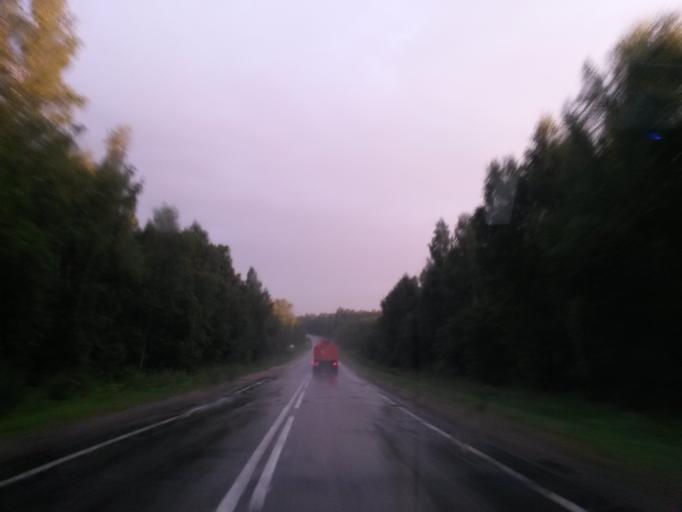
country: RU
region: Jaroslavl
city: Gavrilov-Yam
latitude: 57.3888
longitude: 39.9140
